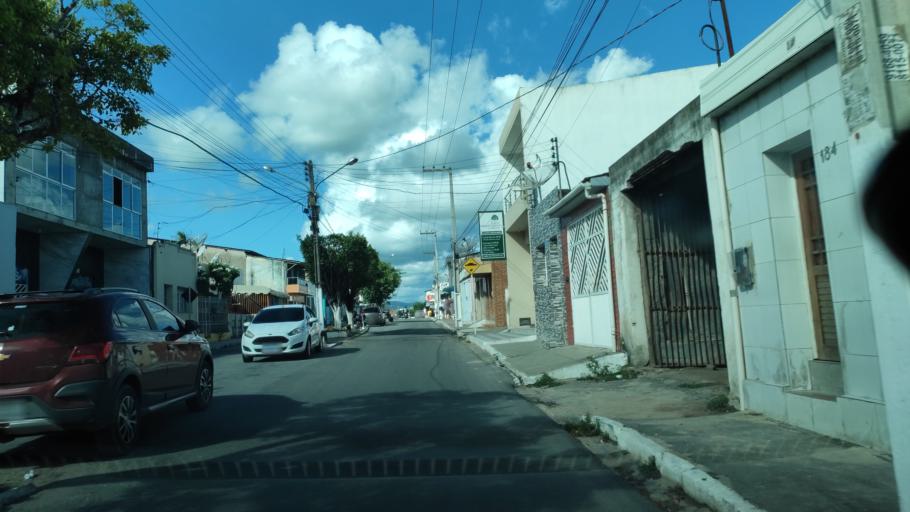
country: BR
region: Alagoas
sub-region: Uniao Dos Palmares
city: Uniao dos Palmares
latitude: -9.1559
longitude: -36.0316
